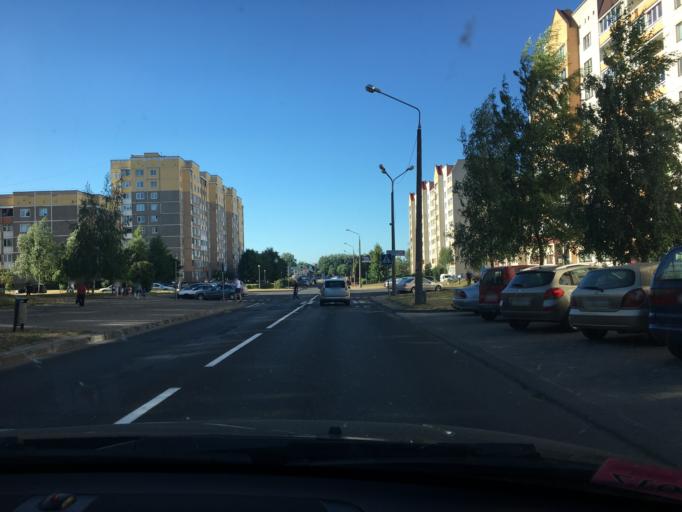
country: BY
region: Grodnenskaya
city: Hrodna
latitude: 53.7131
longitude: 23.8496
